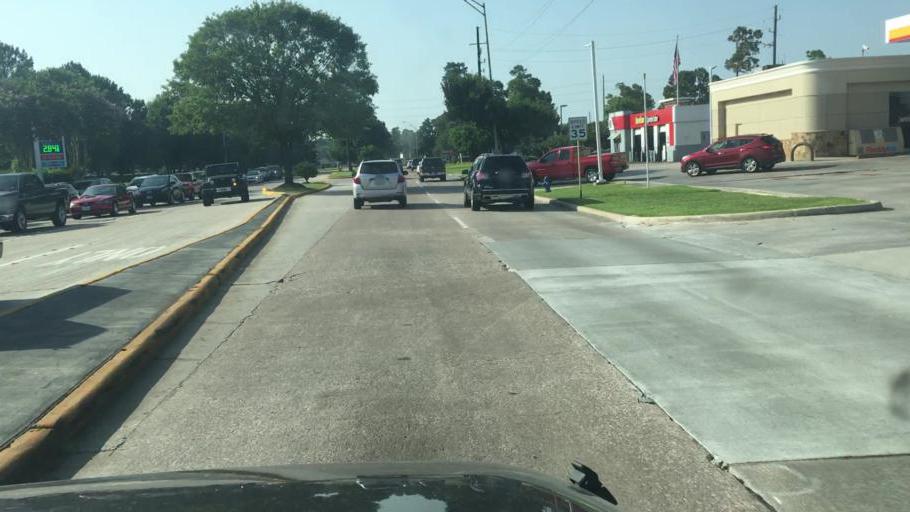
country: US
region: Texas
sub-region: Harris County
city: Atascocita
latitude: 29.9988
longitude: -95.1623
